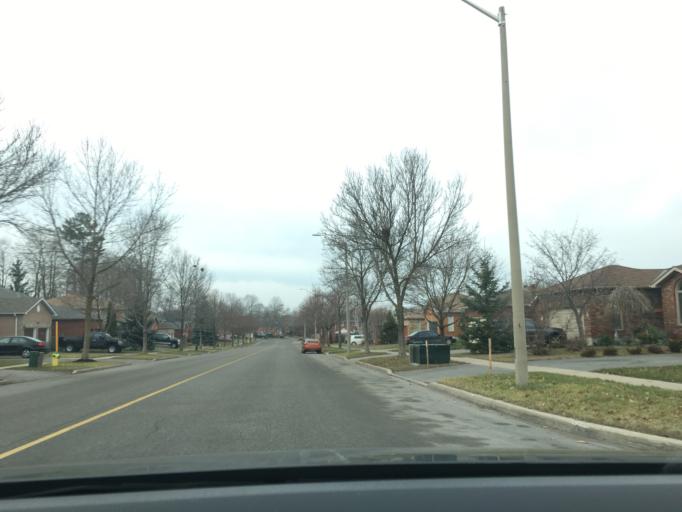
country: CA
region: Ontario
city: Barrie
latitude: 44.3987
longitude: -79.7264
